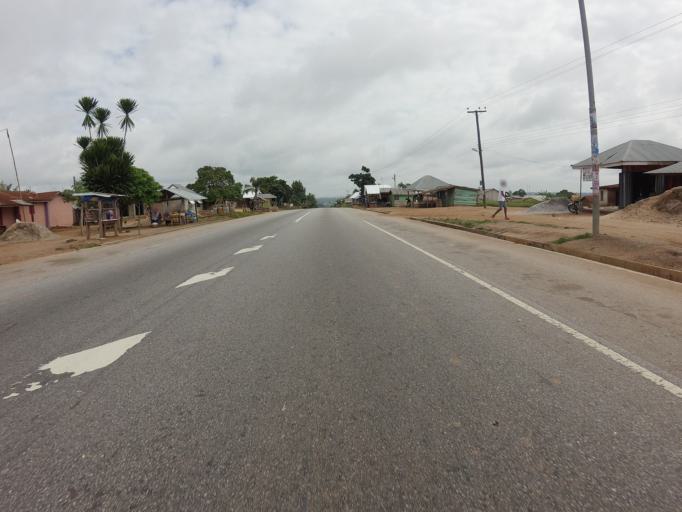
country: GH
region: Ashanti
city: Tafo
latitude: 6.9942
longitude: -1.6953
